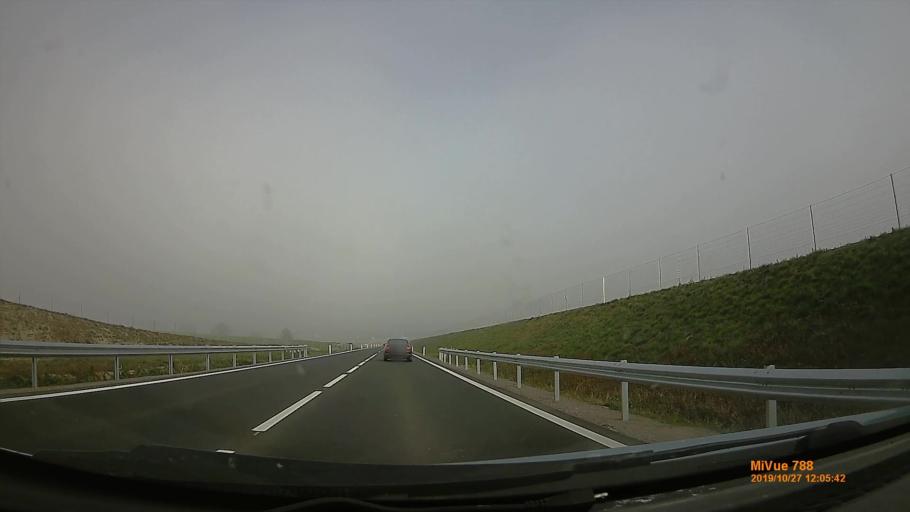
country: AT
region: Lower Austria
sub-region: Politischer Bezirk Mistelbach
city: Drasenhofen
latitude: 48.7664
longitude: 16.6383
